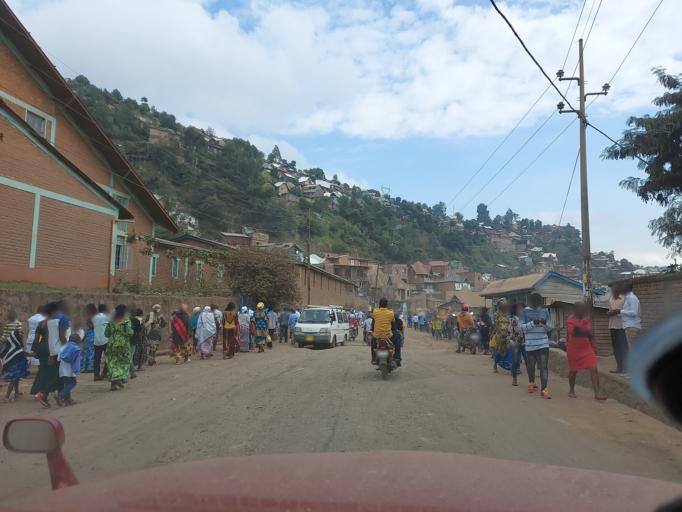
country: CD
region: South Kivu
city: Bukavu
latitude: -2.5114
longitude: 28.8485
